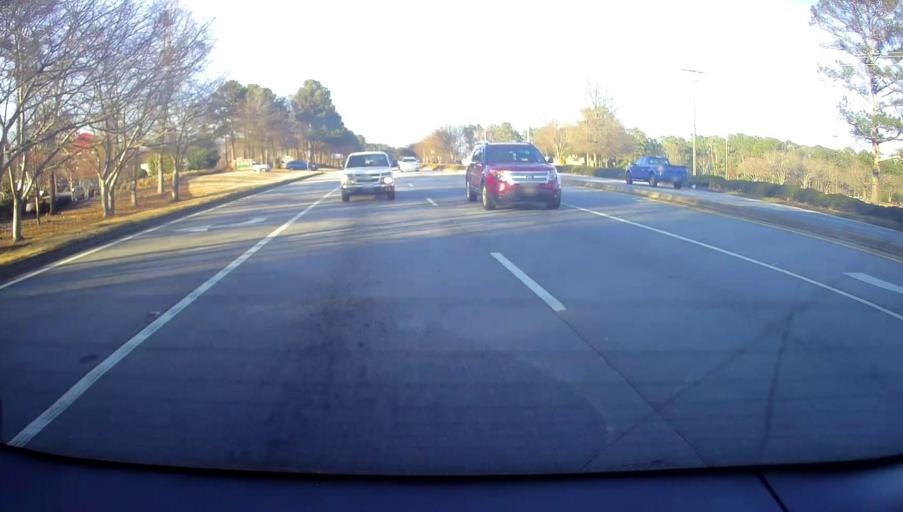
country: US
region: Georgia
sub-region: Fayette County
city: Peachtree City
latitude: 33.4194
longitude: -84.5591
